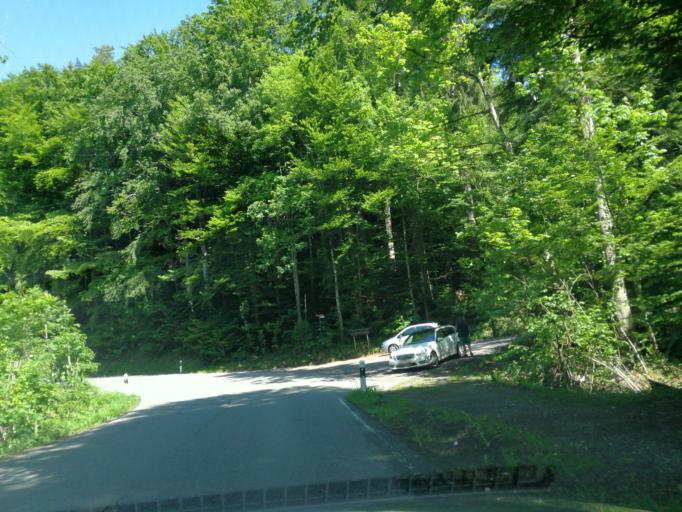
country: CH
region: Saint Gallen
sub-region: Wahlkreis See-Gaster
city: Eschenbach
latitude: 47.2272
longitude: 8.9234
